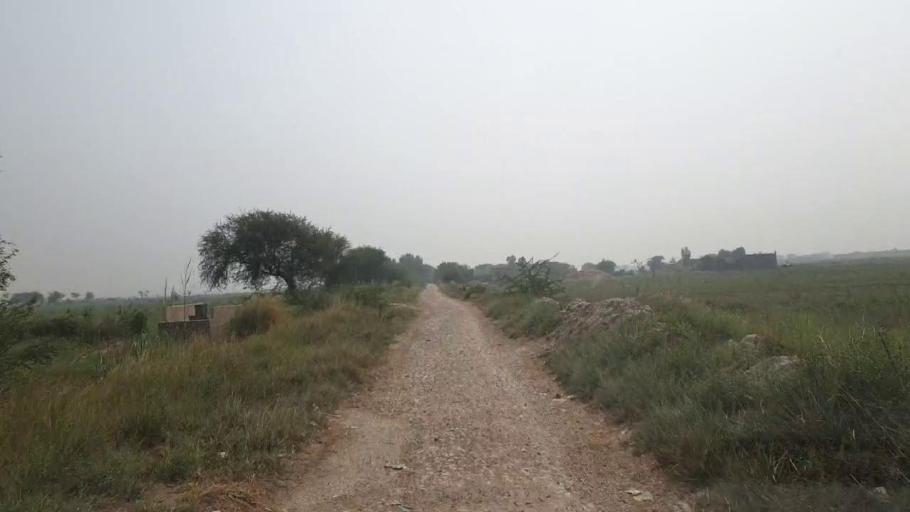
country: PK
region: Sindh
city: Kario
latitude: 24.6523
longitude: 68.6016
